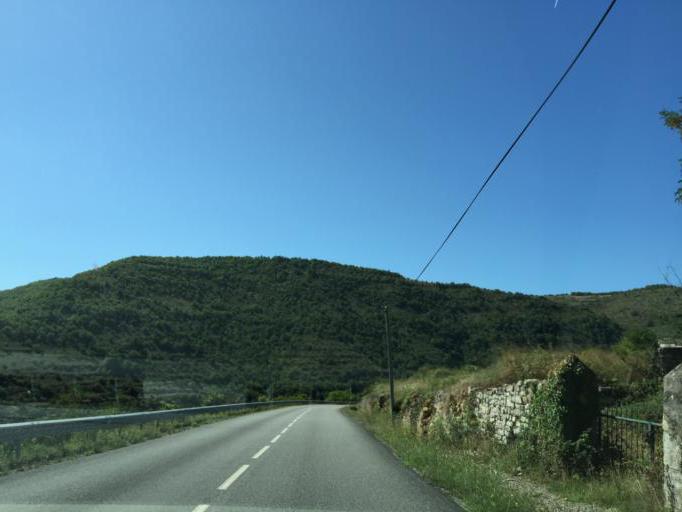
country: FR
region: Midi-Pyrenees
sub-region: Departement de l'Aveyron
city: Saint-Georges-de-Luzencon
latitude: 44.0603
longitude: 2.9148
